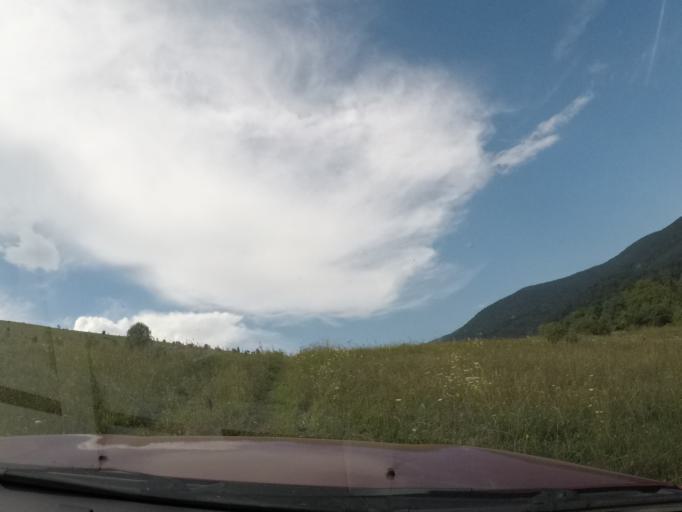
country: UA
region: Zakarpattia
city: Velykyi Bereznyi
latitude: 49.0307
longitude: 22.6383
